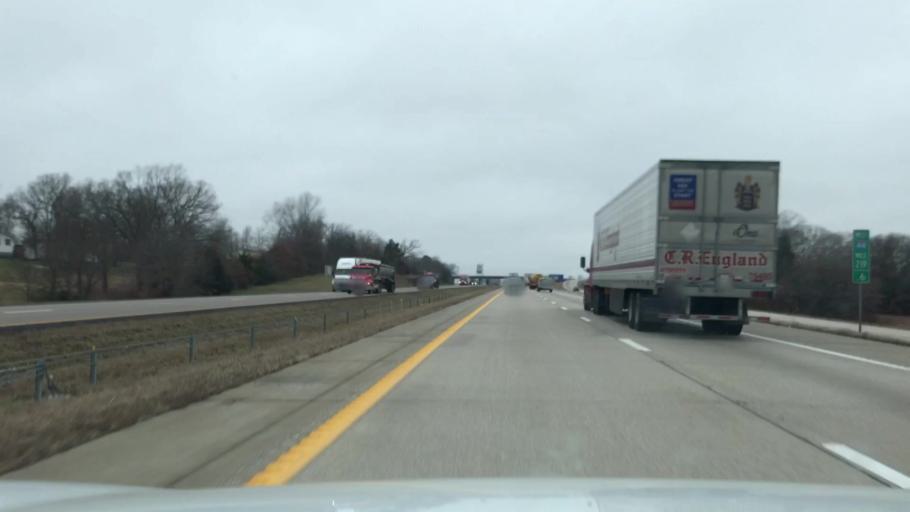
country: US
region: Missouri
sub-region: Crawford County
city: Bourbon
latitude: 38.1611
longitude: -91.2363
